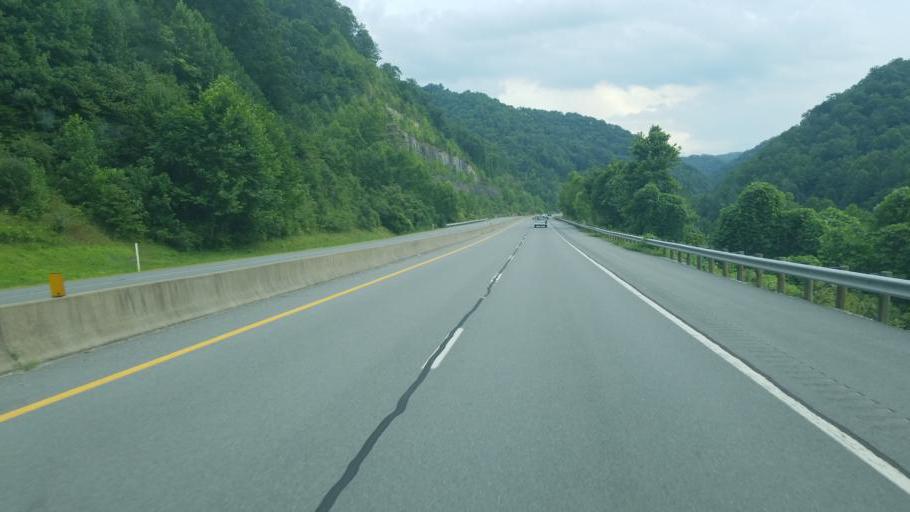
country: US
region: West Virginia
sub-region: Logan County
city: Mount Gay-Shamrock
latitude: 37.8224
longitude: -82.0587
